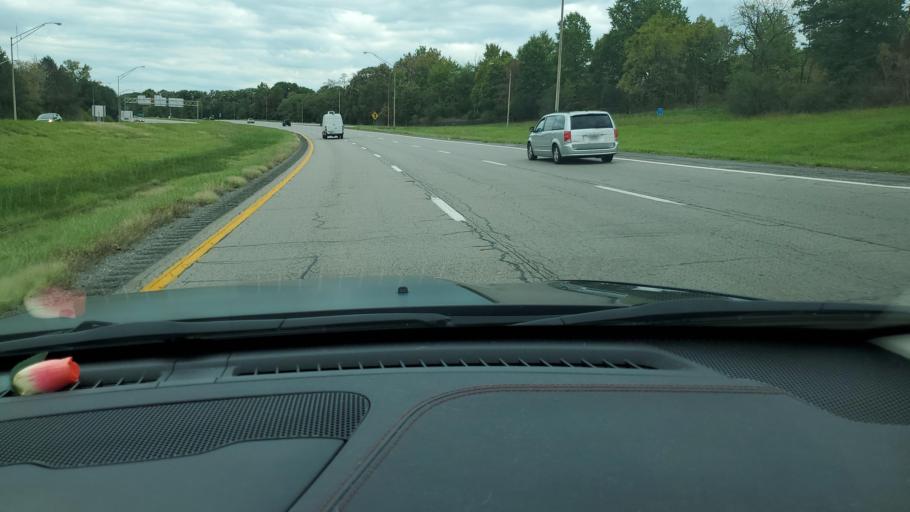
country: US
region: Ohio
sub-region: Mahoning County
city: Poland
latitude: 41.0248
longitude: -80.6265
